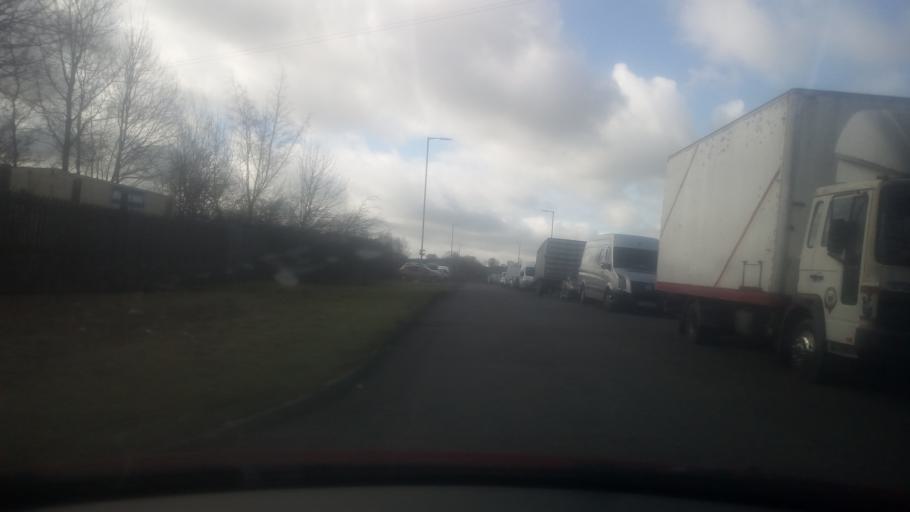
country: GB
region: Scotland
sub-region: The Scottish Borders
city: Saint Boswells
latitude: 55.5575
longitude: -2.6548
